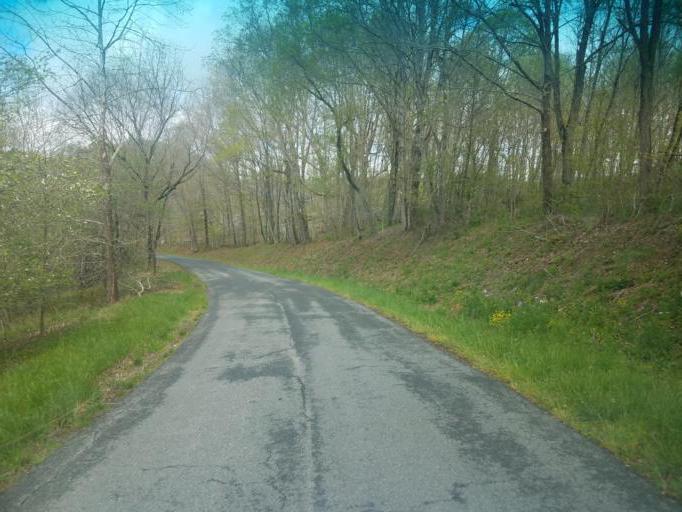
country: US
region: Virginia
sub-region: Smyth County
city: Atkins
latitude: 36.9741
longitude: -81.3925
